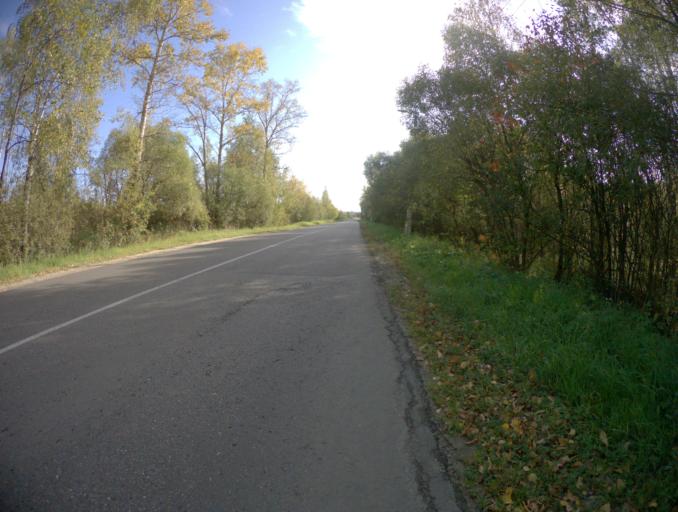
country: RU
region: Moskovskaya
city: Roshal'
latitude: 55.6582
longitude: 39.8367
